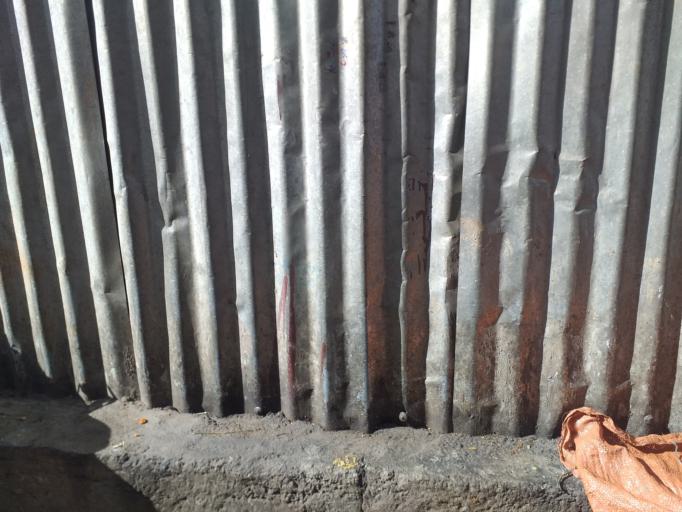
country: ET
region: Adis Abeba
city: Addis Ababa
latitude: 9.0247
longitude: 38.8210
